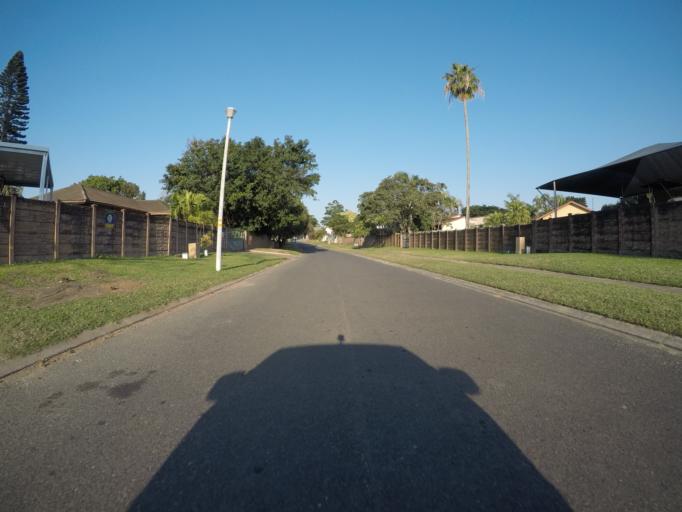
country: ZA
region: KwaZulu-Natal
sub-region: uThungulu District Municipality
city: Richards Bay
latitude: -28.7816
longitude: 32.1101
